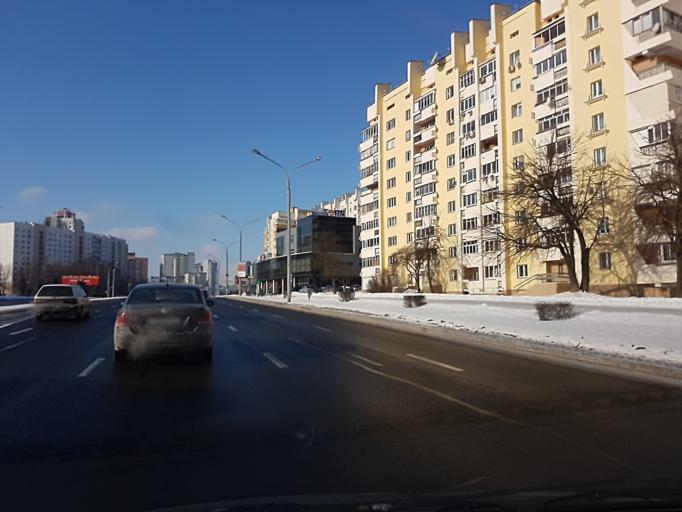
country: BY
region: Minsk
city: Minsk
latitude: 53.9133
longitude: 27.5362
